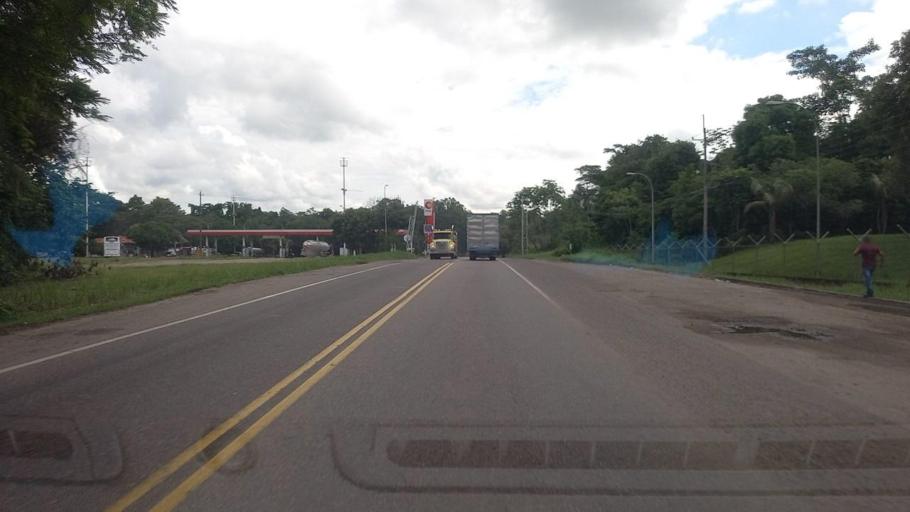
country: CO
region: Santander
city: Sabana de Torres
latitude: 7.1283
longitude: -73.5707
